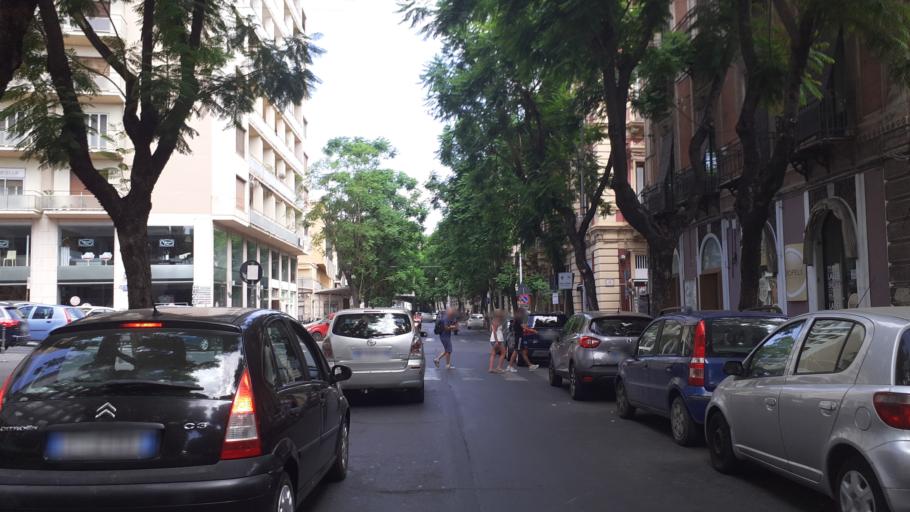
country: IT
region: Sicily
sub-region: Catania
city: Catania
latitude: 37.5090
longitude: 15.0849
